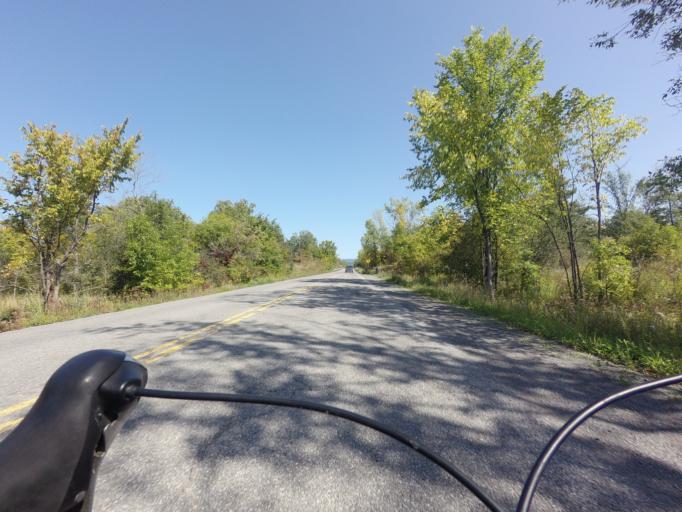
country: CA
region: Ontario
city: Bells Corners
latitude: 45.4034
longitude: -76.0496
